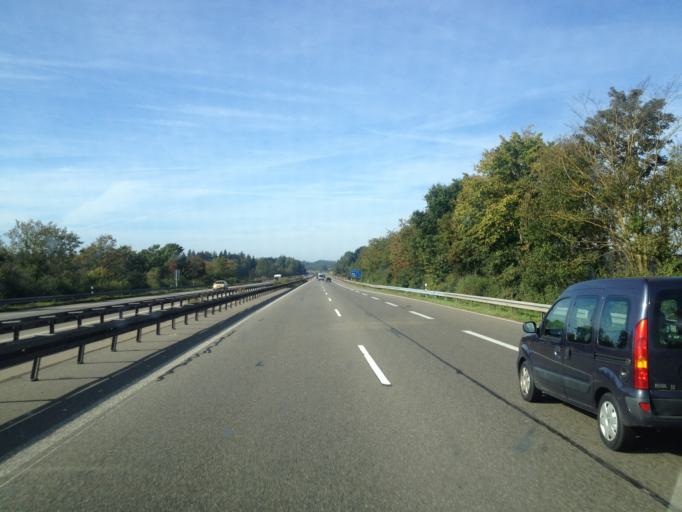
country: DE
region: Baden-Wuerttemberg
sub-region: Freiburg Region
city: Dietingen
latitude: 48.2040
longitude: 8.6180
